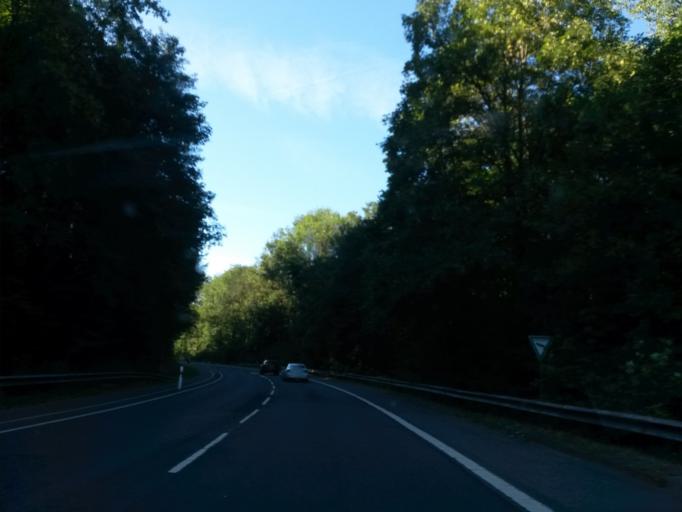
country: DE
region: North Rhine-Westphalia
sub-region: Regierungsbezirk Koln
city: Engelskirchen
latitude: 51.0139
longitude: 7.4347
